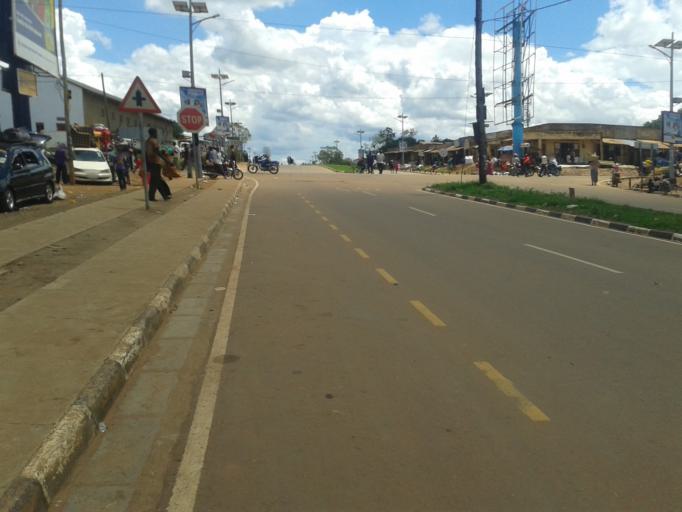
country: UG
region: Northern Region
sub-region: Gulu District
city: Gulu
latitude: 2.7643
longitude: 32.3003
